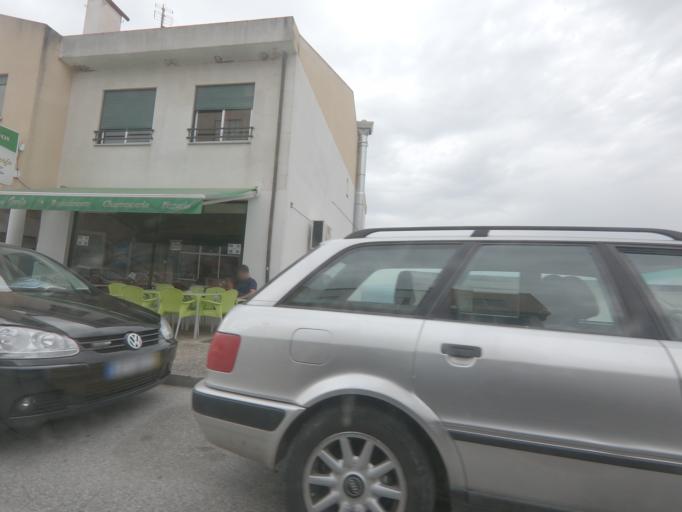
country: PT
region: Viseu
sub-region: Armamar
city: Armamar
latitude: 41.1097
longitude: -7.6903
